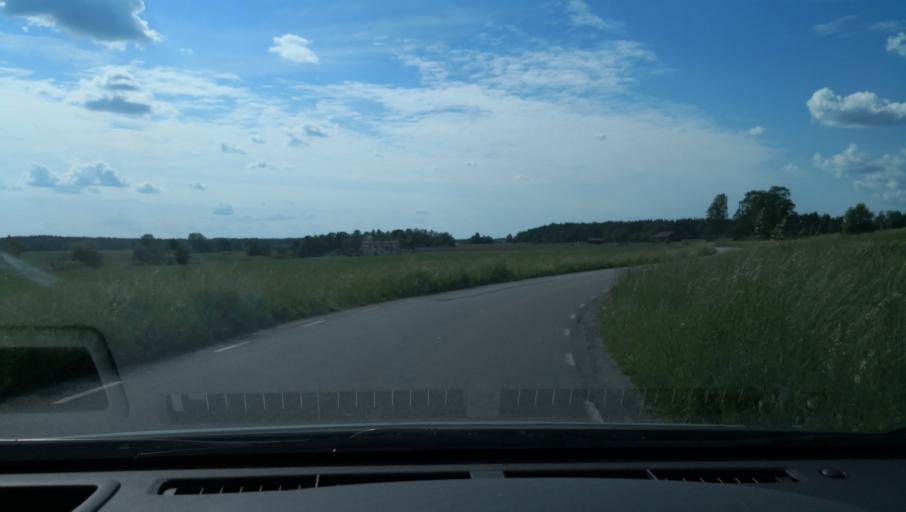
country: SE
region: Uppsala
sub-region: Enkopings Kommun
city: Orsundsbro
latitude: 59.8156
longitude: 17.3560
